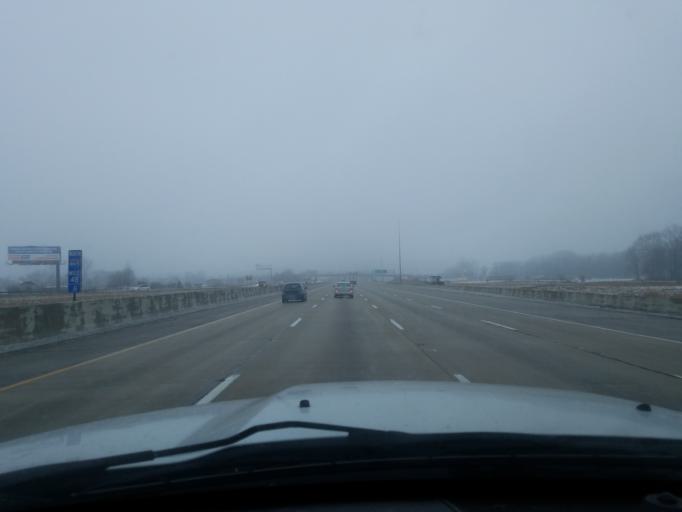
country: US
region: Indiana
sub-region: Marion County
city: Beech Grove
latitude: 39.7342
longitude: -86.0437
